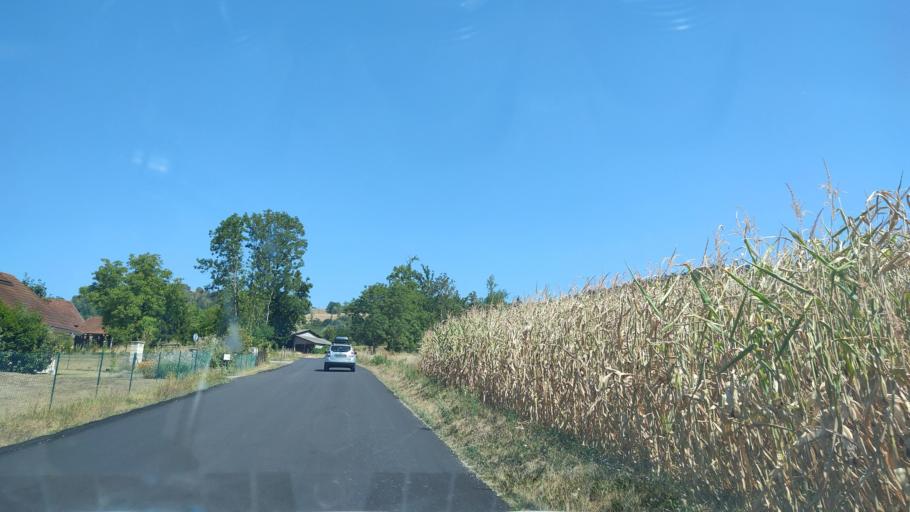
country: FR
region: Rhone-Alpes
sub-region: Departement de la Savoie
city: Novalaise
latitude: 45.5964
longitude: 5.7787
